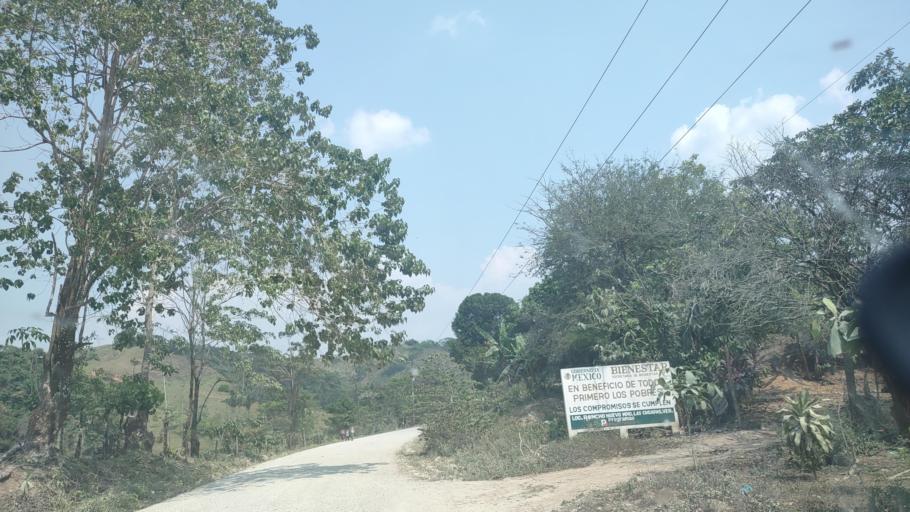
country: MX
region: Tabasco
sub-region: Huimanguillo
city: Francisco Rueda
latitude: 17.5926
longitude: -93.8957
